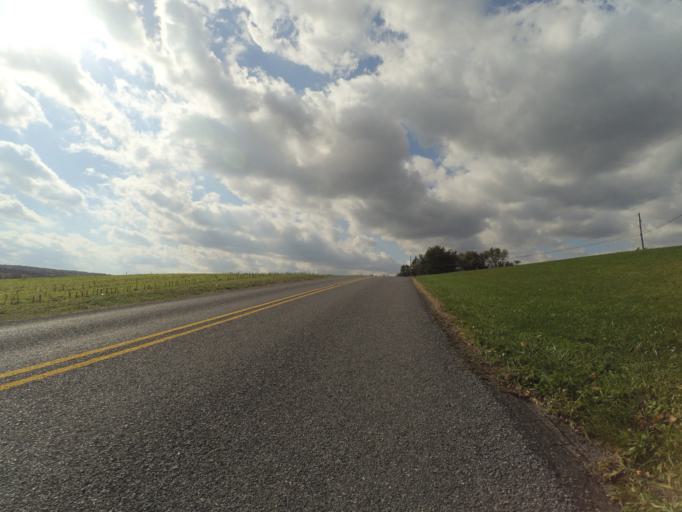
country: US
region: Pennsylvania
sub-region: Centre County
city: Bellefonte
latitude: 40.8872
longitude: -77.8091
